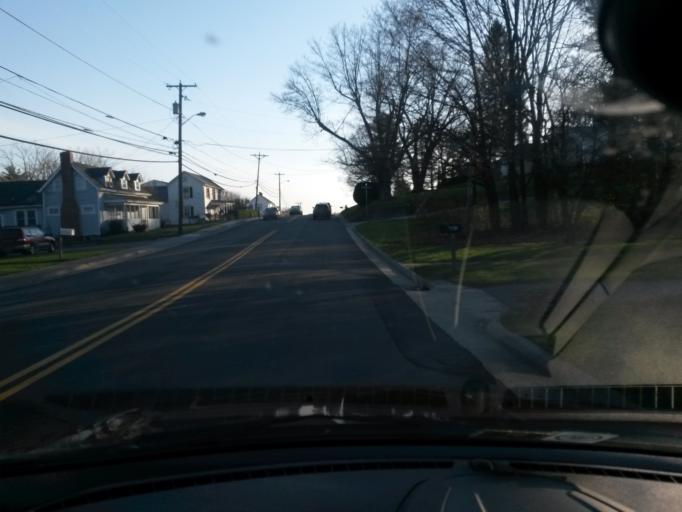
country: US
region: Virginia
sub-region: Montgomery County
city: Christiansburg
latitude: 37.1244
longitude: -80.4152
